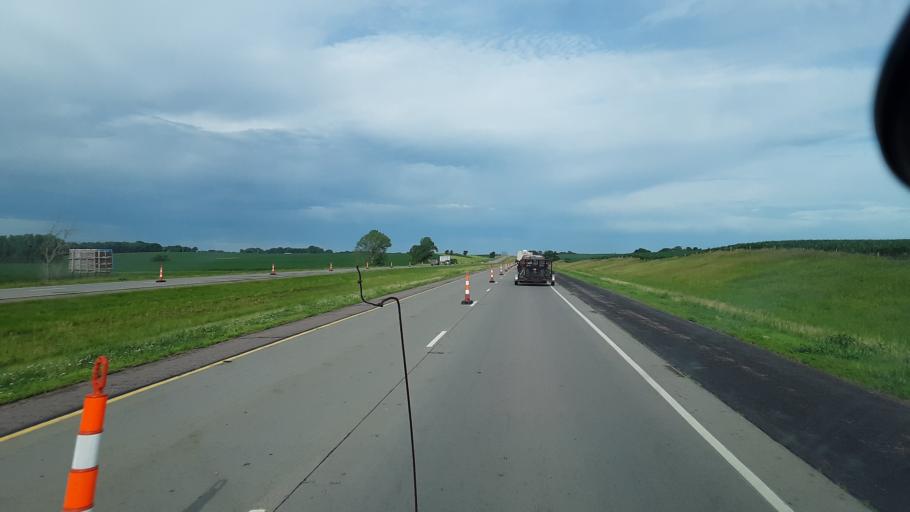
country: US
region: South Dakota
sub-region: Minnehaha County
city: Crooks
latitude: 43.6088
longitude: -96.8338
